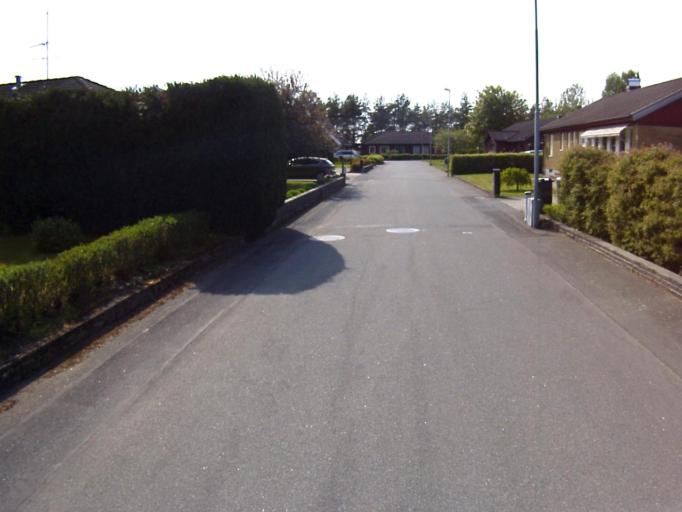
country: SE
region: Skane
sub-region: Kristianstads Kommun
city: Onnestad
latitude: 56.0605
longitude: 14.0872
